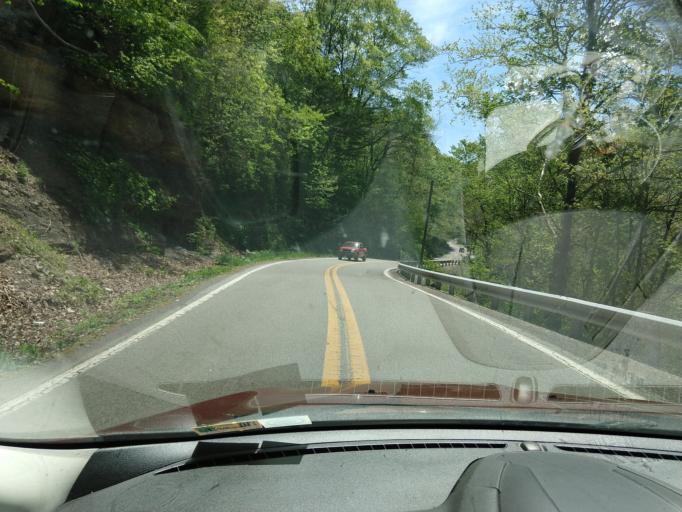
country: US
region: West Virginia
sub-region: McDowell County
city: Welch
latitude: 37.3188
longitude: -81.6949
